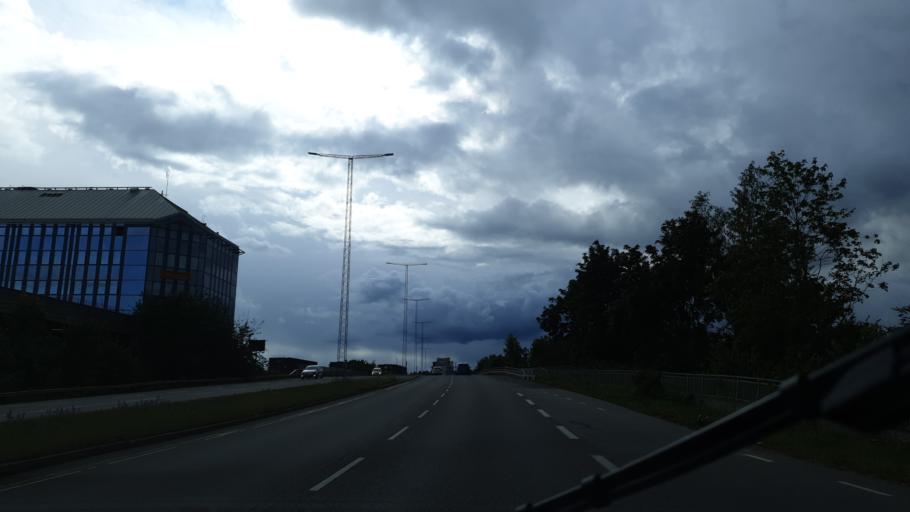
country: SE
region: Stockholm
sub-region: Jarfalla Kommun
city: Jakobsberg
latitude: 59.4255
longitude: 17.8352
